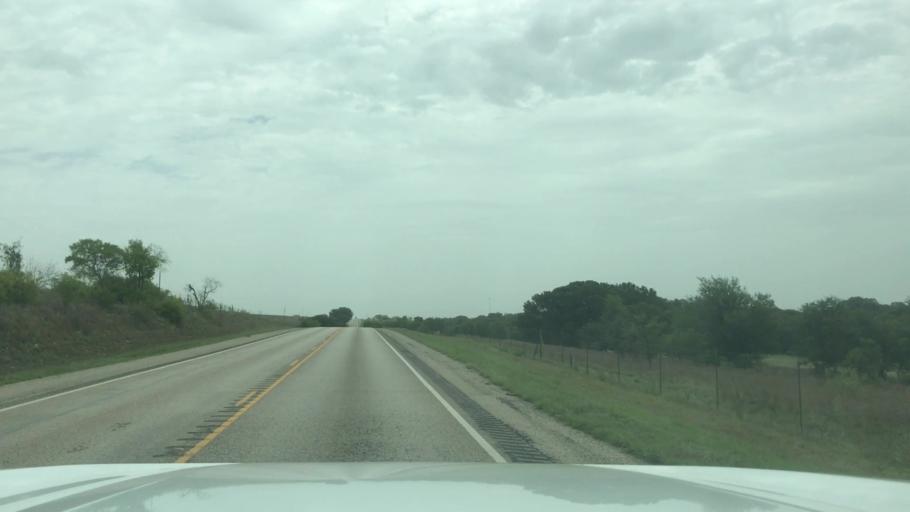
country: US
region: Texas
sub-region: Erath County
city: Dublin
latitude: 32.0562
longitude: -98.1825
